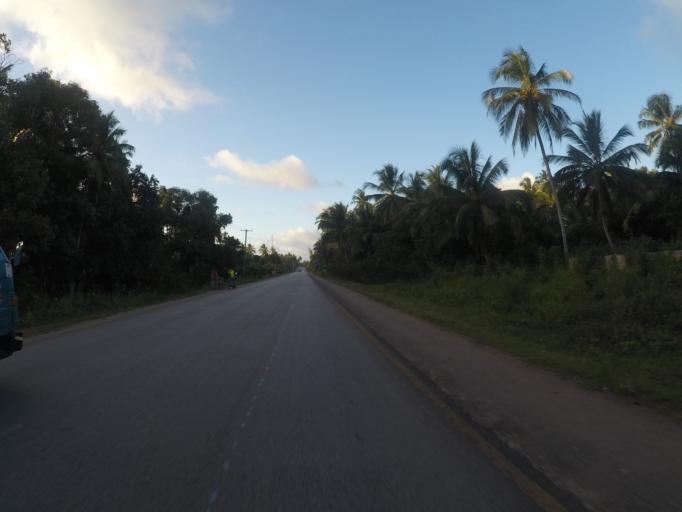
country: TZ
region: Zanzibar Central/South
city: Koani
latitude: -6.1277
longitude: 39.3258
